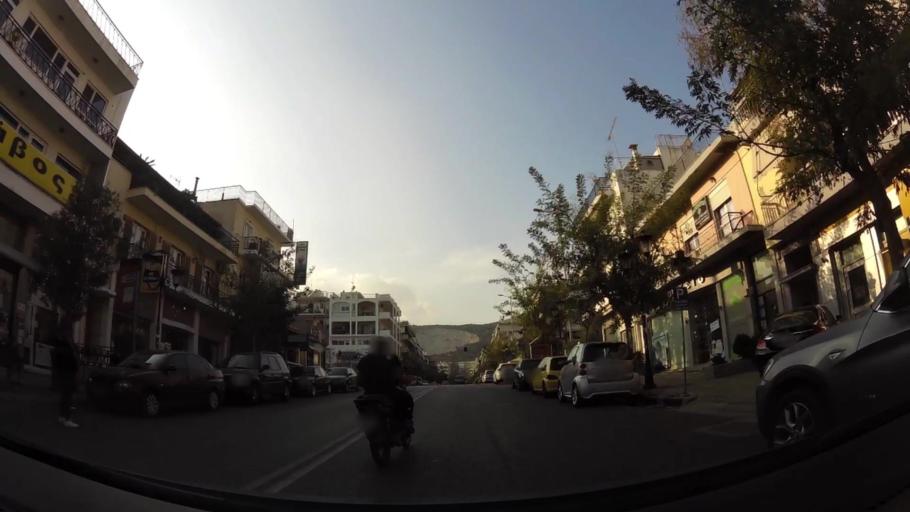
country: GR
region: Attica
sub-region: Nomarchia Athinas
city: Petroupolis
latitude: 38.0429
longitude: 23.6828
